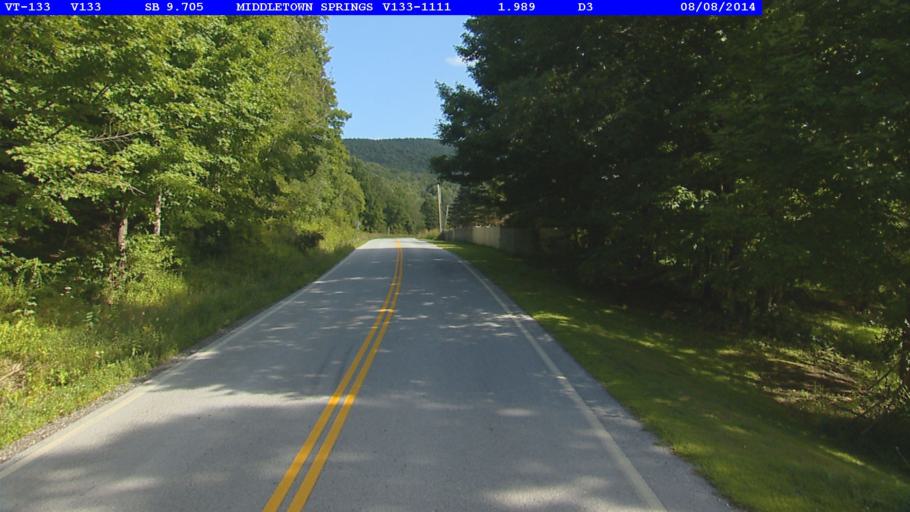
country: US
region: Vermont
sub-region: Rutland County
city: Poultney
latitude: 43.4635
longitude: -73.1126
